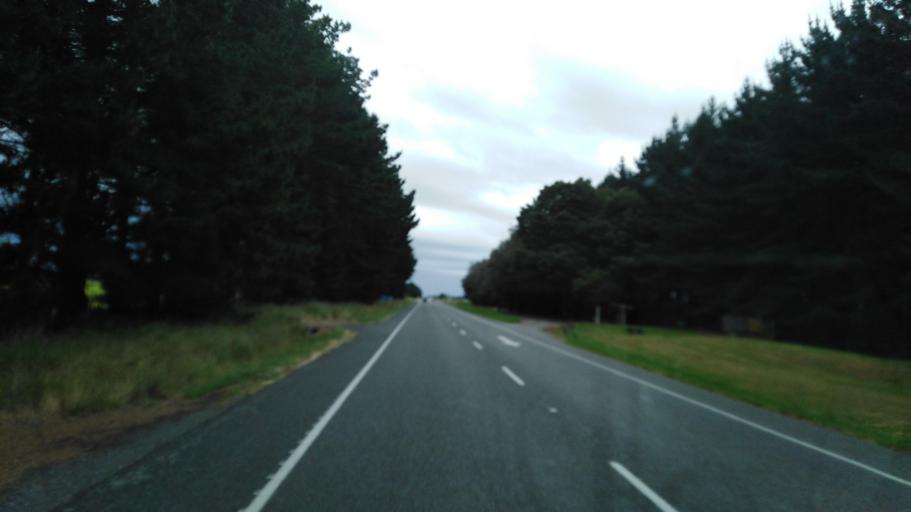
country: NZ
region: Manawatu-Wanganui
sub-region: Horowhenua District
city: Foxton
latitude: -40.4178
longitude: 175.3060
